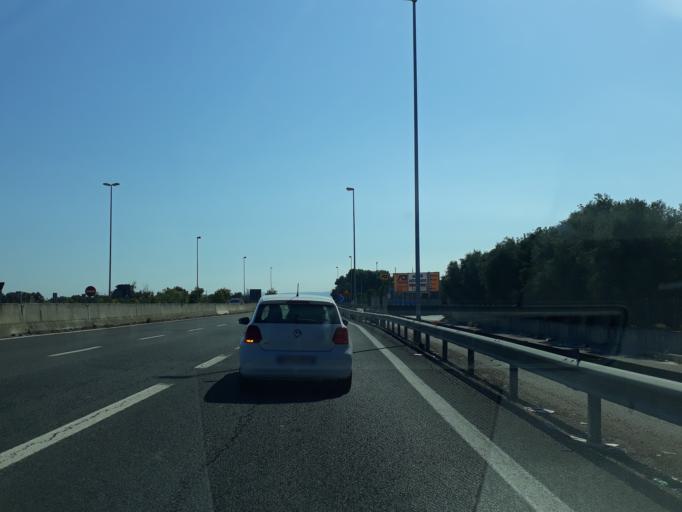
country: IT
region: Apulia
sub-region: Provincia di Bari
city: Monopoli
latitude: 40.9181
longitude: 17.3183
